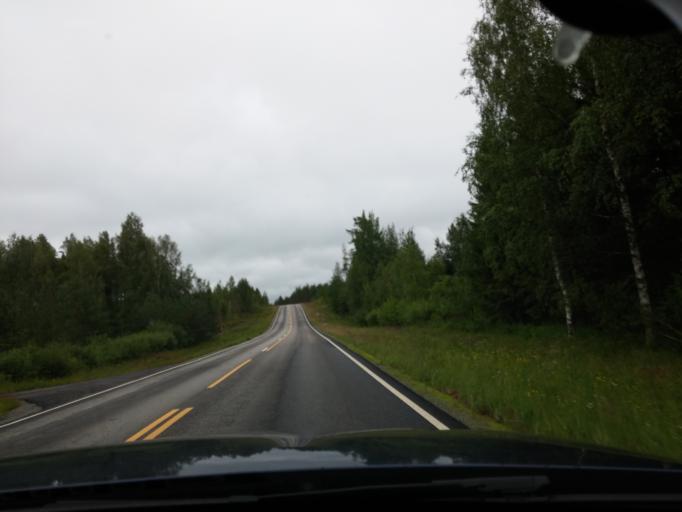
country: FI
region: Central Finland
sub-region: Saarijaervi-Viitasaari
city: Pylkoenmaeki
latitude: 62.6409
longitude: 24.8455
